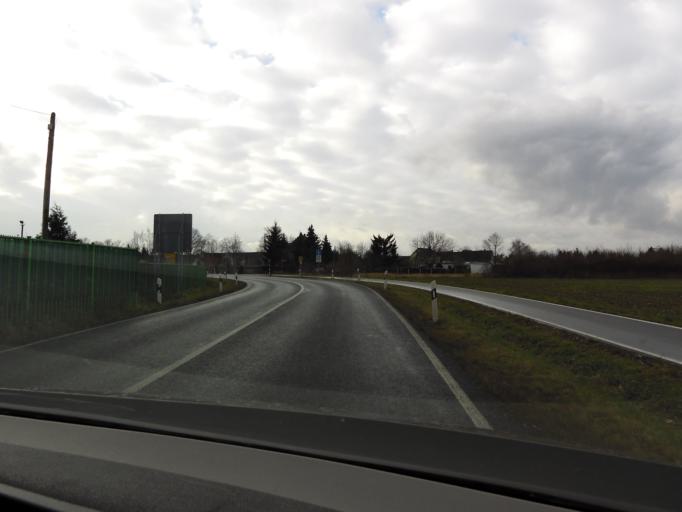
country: DE
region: Saxony
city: Kitzen
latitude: 51.2555
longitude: 12.2764
